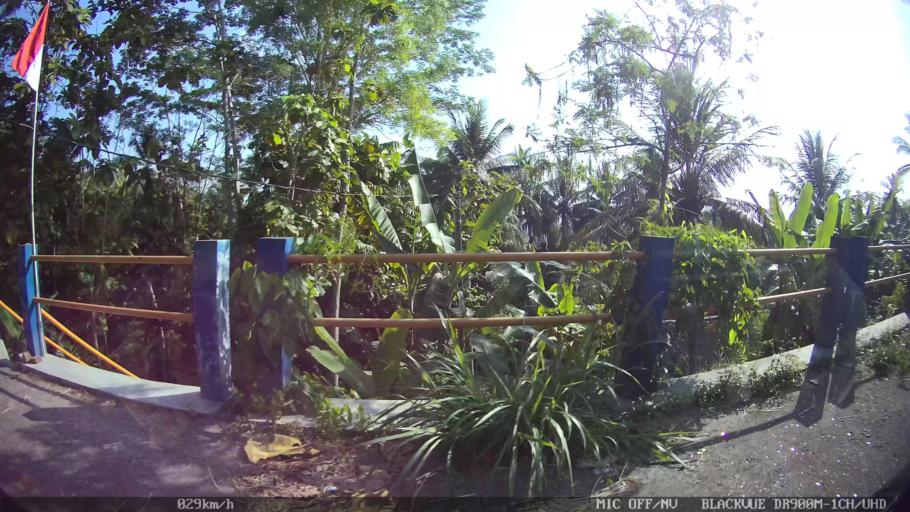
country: ID
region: Daerah Istimewa Yogyakarta
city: Kasihan
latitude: -7.8342
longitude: 110.2761
